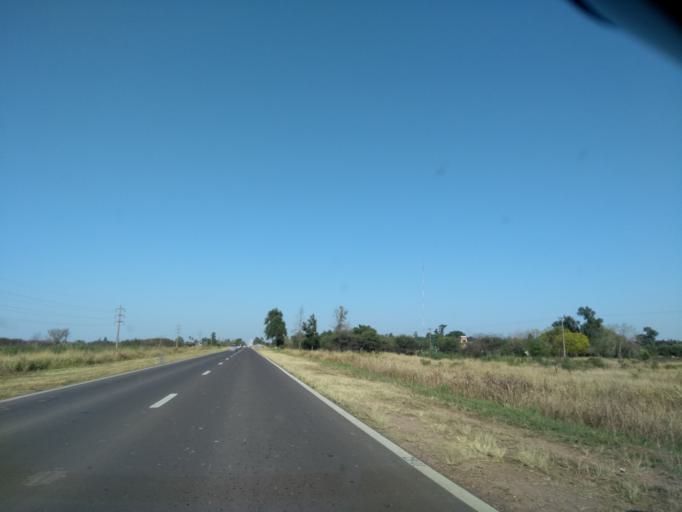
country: AR
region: Chaco
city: Presidencia Roque Saenz Pena
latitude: -26.7715
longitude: -60.4004
